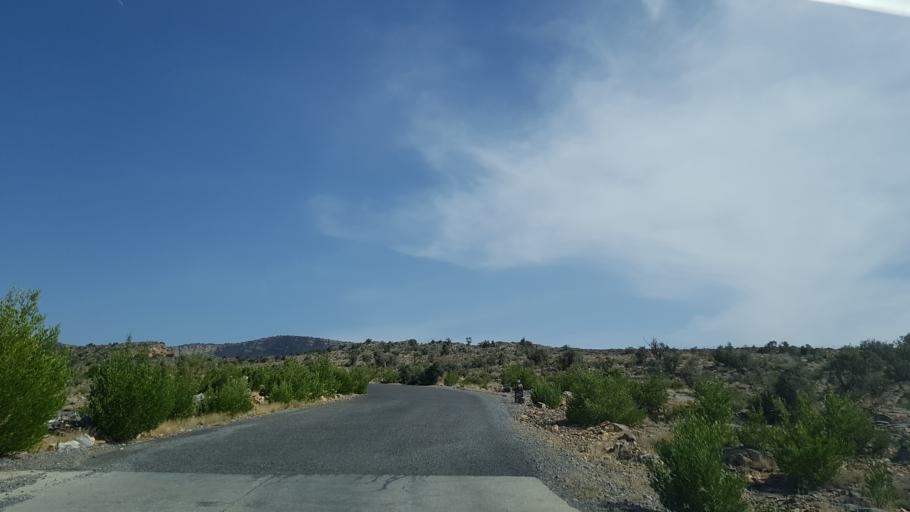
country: OM
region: Al Batinah
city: Bayt al `Awabi
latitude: 23.1415
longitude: 57.5372
